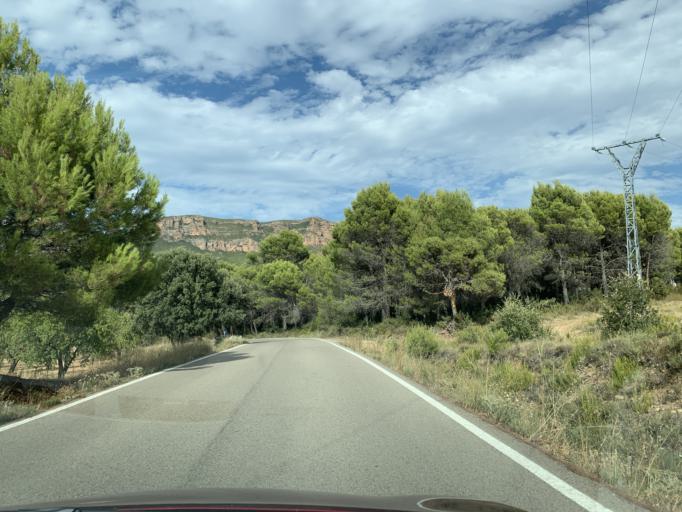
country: ES
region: Aragon
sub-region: Provincia de Zaragoza
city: Santa Eulalia de Gallego
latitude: 42.3182
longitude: -0.7265
